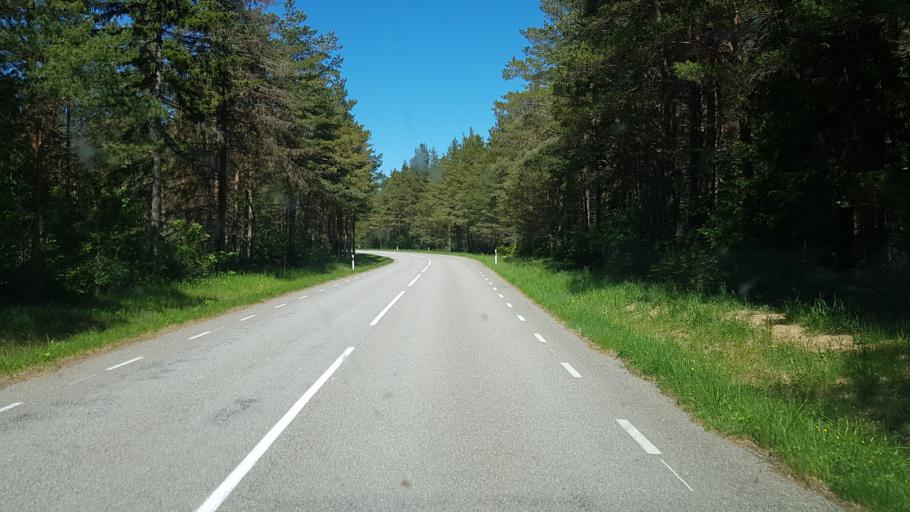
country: EE
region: Saare
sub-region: Kuressaare linn
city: Kuressaare
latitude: 58.0050
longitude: 22.1670
